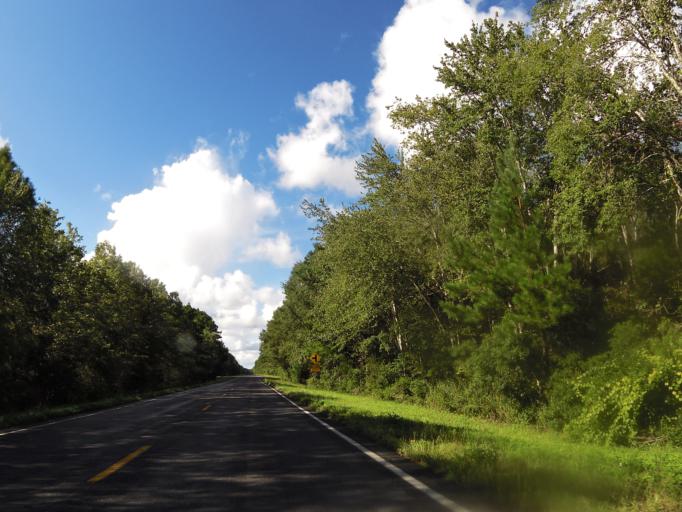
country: US
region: Georgia
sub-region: Camden County
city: Woodbine
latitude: 30.9827
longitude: -81.7279
